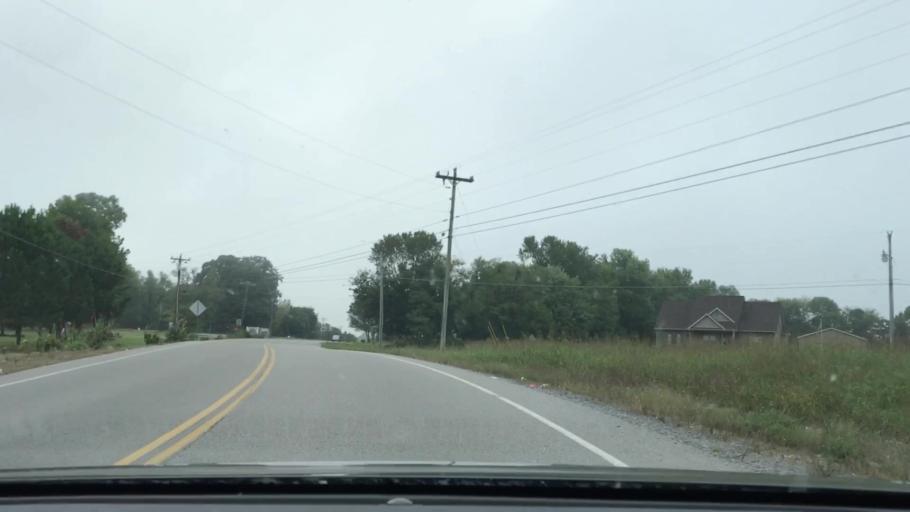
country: US
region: Tennessee
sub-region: Sumner County
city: Portland
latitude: 36.4893
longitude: -86.4928
